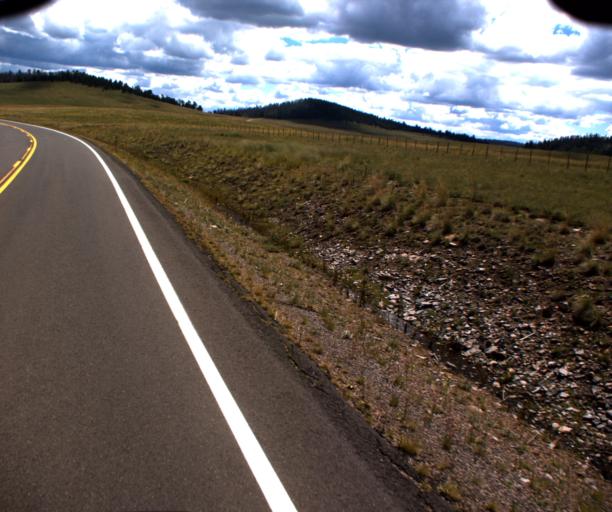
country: US
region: Arizona
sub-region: Apache County
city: Eagar
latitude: 33.9204
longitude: -109.4371
